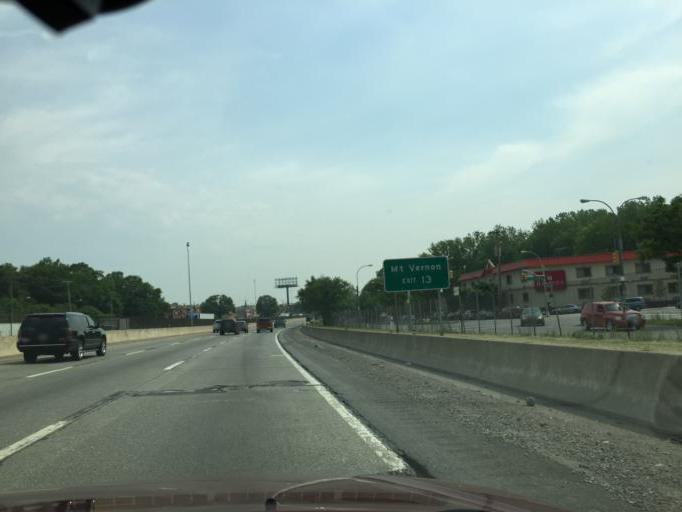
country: US
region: New York
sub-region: Bronx
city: Eastchester
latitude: 40.8795
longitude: -73.8326
